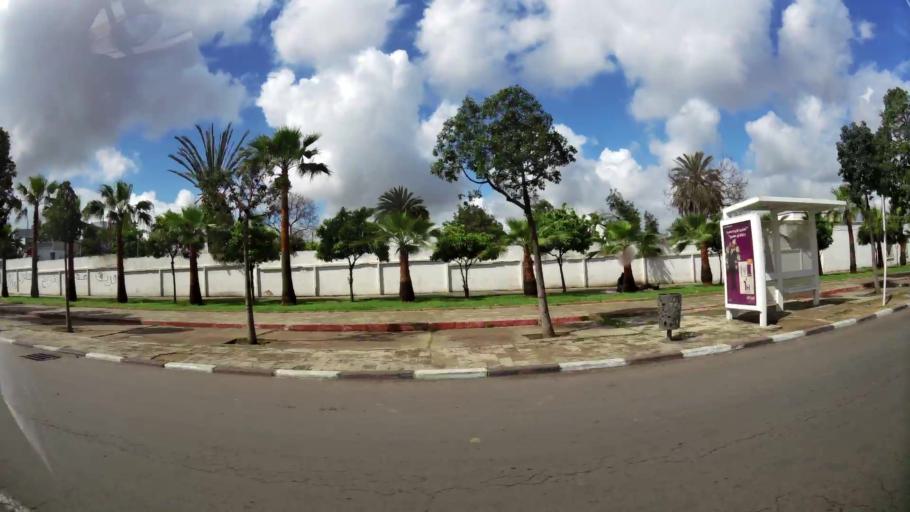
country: MA
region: Grand Casablanca
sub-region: Casablanca
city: Casablanca
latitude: 33.5546
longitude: -7.5924
